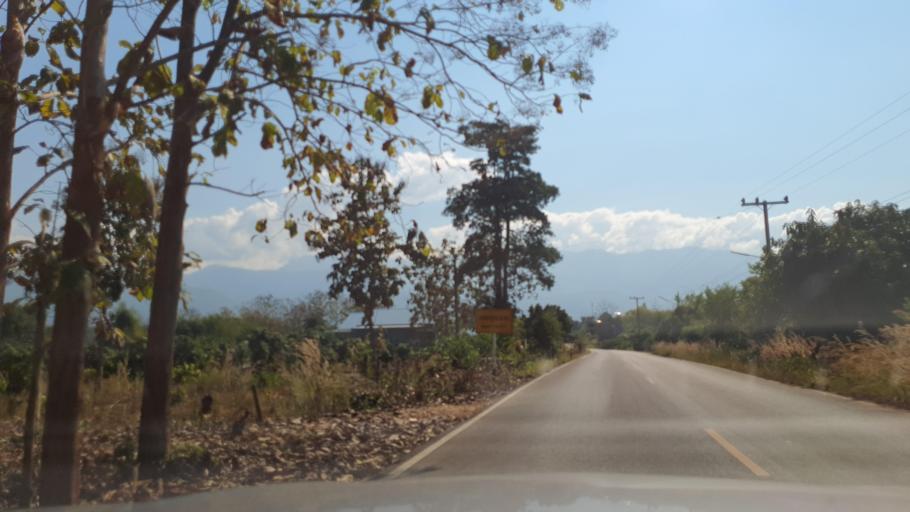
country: TH
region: Nan
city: Pua
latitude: 19.1500
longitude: 100.9147
